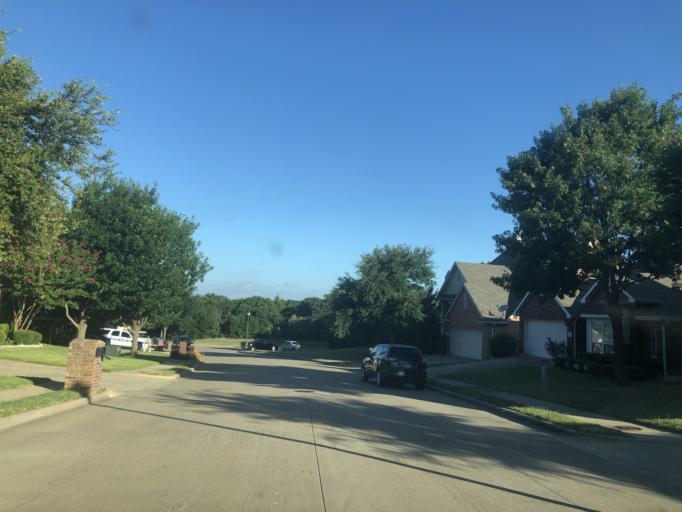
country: US
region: Texas
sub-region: Dallas County
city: Duncanville
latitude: 32.6599
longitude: -96.9460
